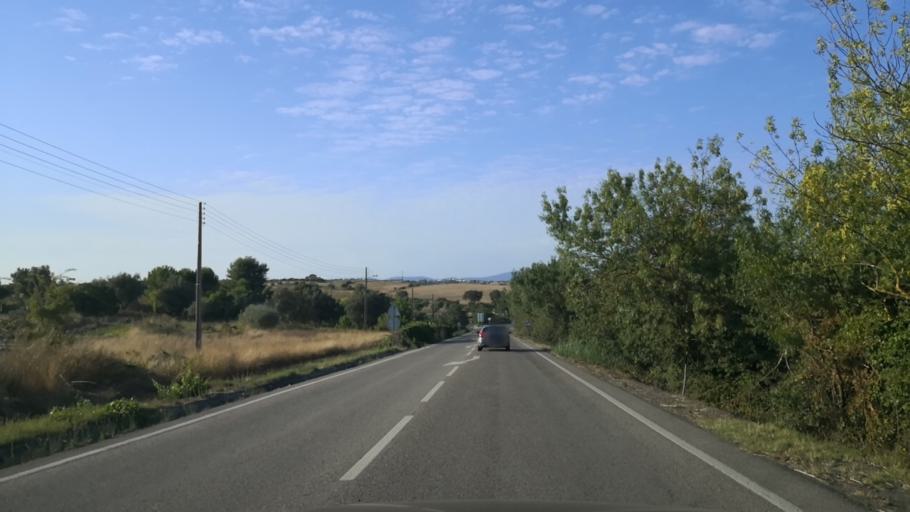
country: PT
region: Santarem
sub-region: Santarem
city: Santarem
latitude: 39.3161
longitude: -8.6702
